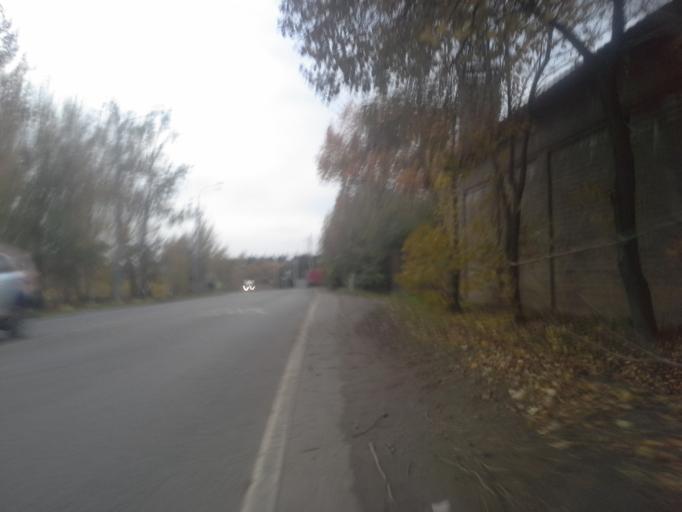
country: RU
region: Moskovskaya
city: Odintsovo
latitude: 55.6452
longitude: 37.2683
